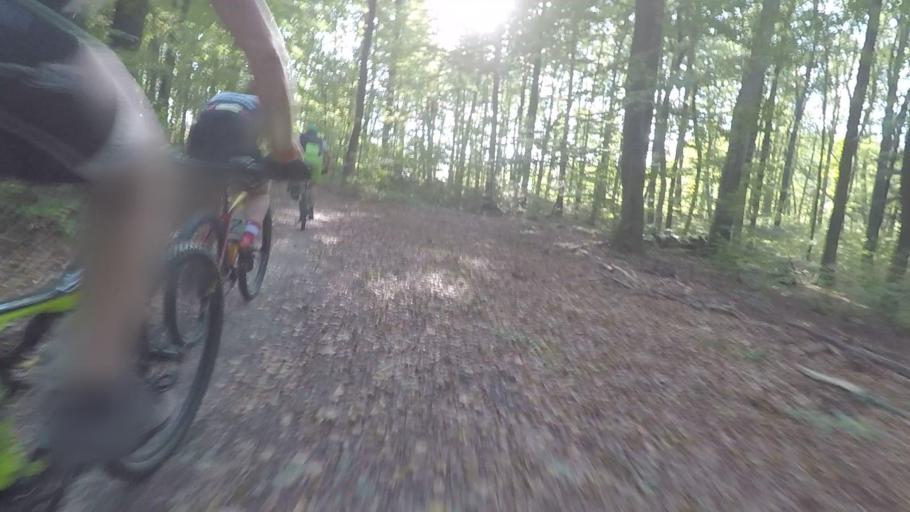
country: DE
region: Baden-Wuerttemberg
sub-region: Regierungsbezirk Stuttgart
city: Grosserlach
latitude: 49.0645
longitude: 9.4932
